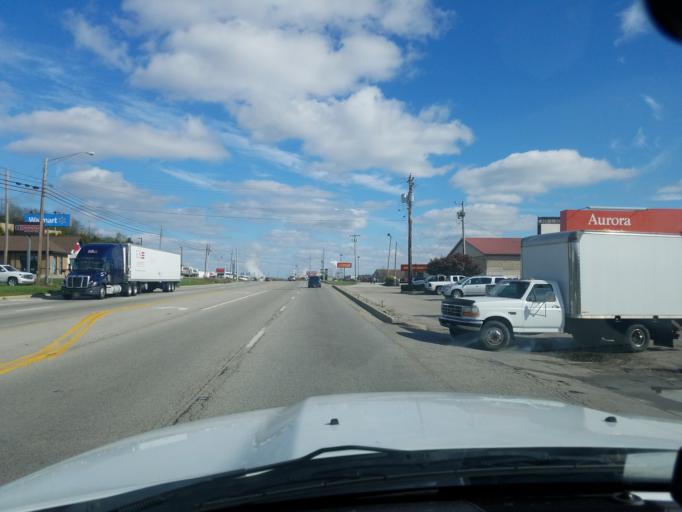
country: US
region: Indiana
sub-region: Dearborn County
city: Aurora
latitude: 39.0776
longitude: -84.8894
